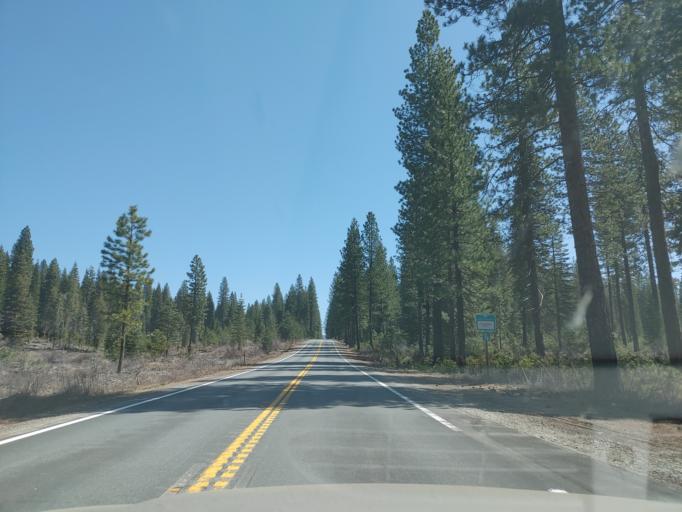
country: US
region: California
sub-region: Siskiyou County
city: McCloud
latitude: 41.2665
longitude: -121.8790
